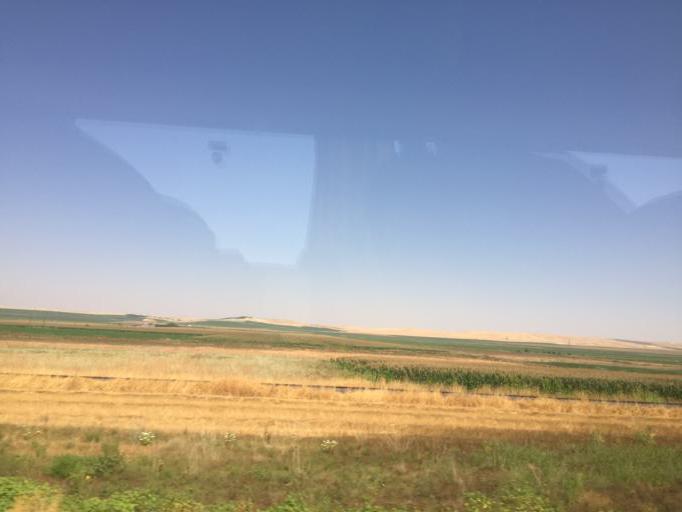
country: TR
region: Diyarbakir
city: Tepe
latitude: 37.8498
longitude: 40.7845
